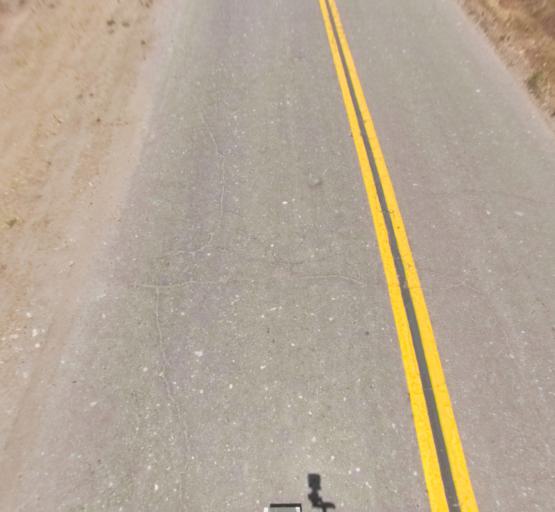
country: US
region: California
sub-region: Fresno County
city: Auberry
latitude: 37.2337
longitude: -119.4997
